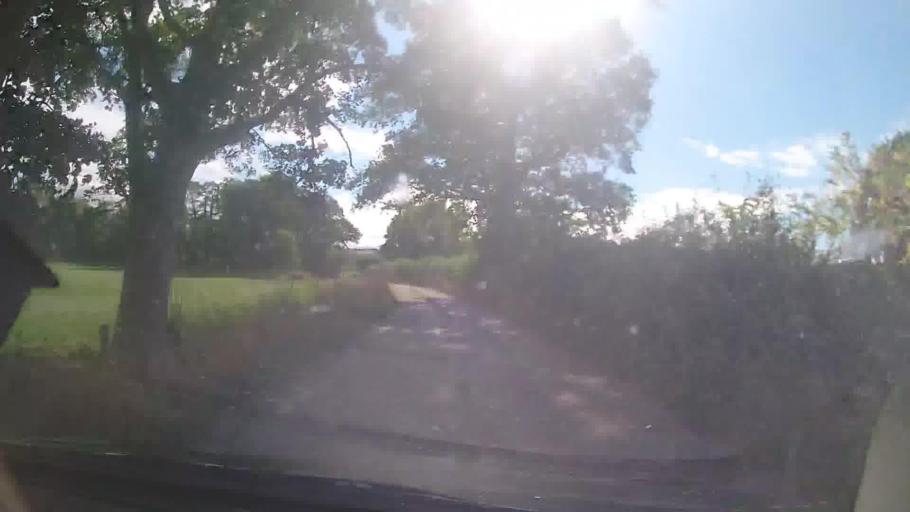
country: GB
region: England
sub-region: Shropshire
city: Prees
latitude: 52.8789
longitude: -2.6296
